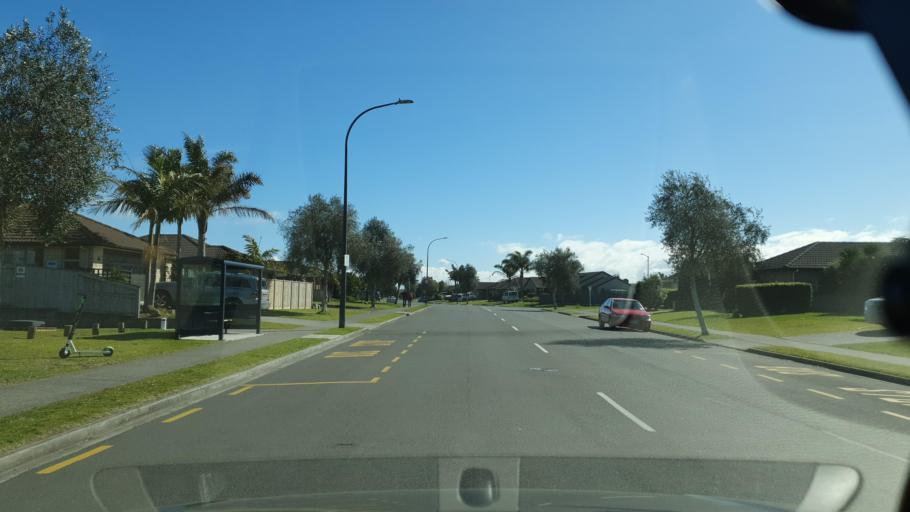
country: NZ
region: Bay of Plenty
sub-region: Tauranga City
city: Tauranga
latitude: -37.7090
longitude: 176.2959
